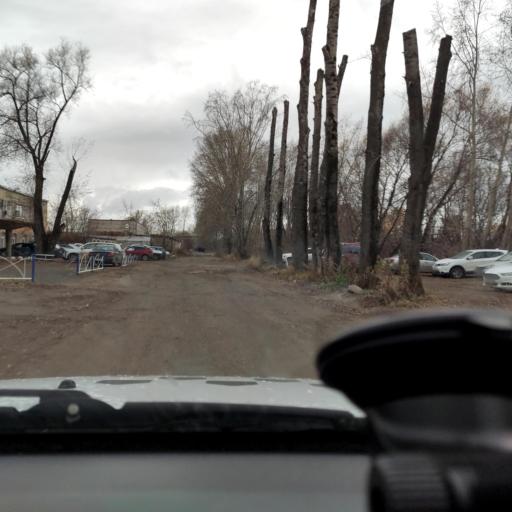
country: RU
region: Perm
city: Kondratovo
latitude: 57.9455
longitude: 56.1409
